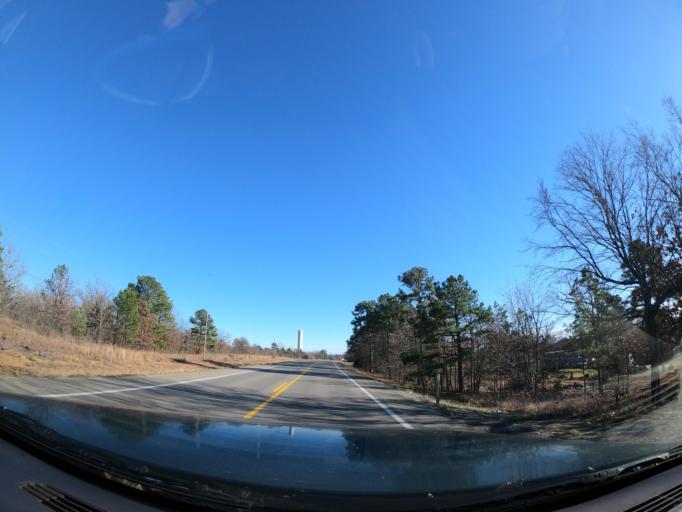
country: US
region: Oklahoma
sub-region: Pittsburg County
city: Longtown
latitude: 35.2305
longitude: -95.4544
